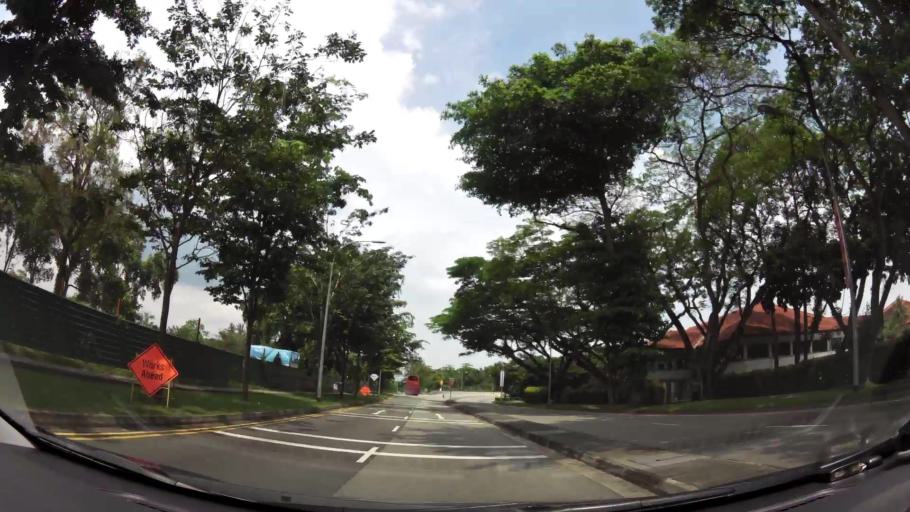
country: MY
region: Johor
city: Kampung Pasir Gudang Baru
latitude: 1.3891
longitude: 103.9900
